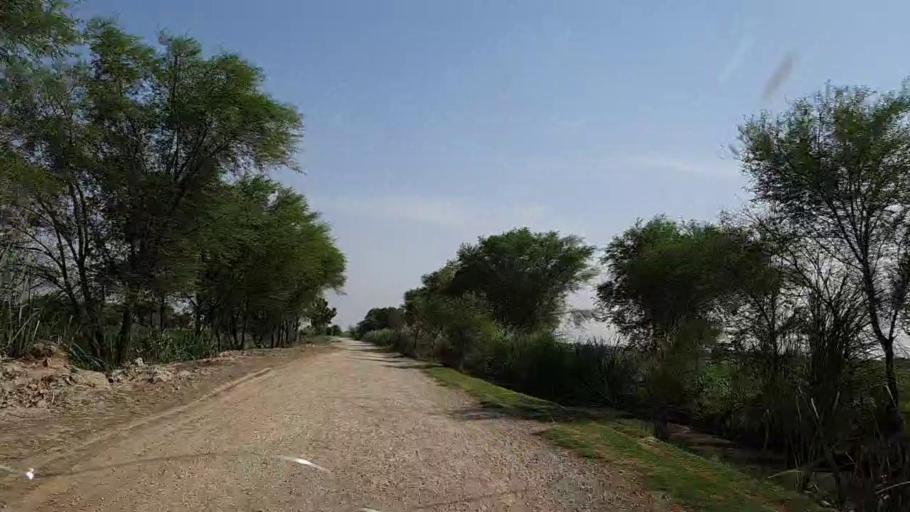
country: PK
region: Sindh
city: Khanpur
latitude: 27.7226
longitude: 69.3605
